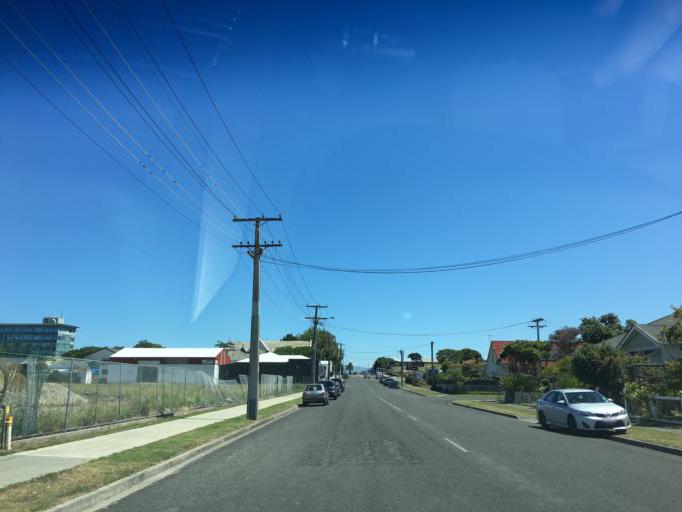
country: NZ
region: Gisborne
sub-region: Gisborne District
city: Gisborne
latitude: -38.6615
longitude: 178.0259
